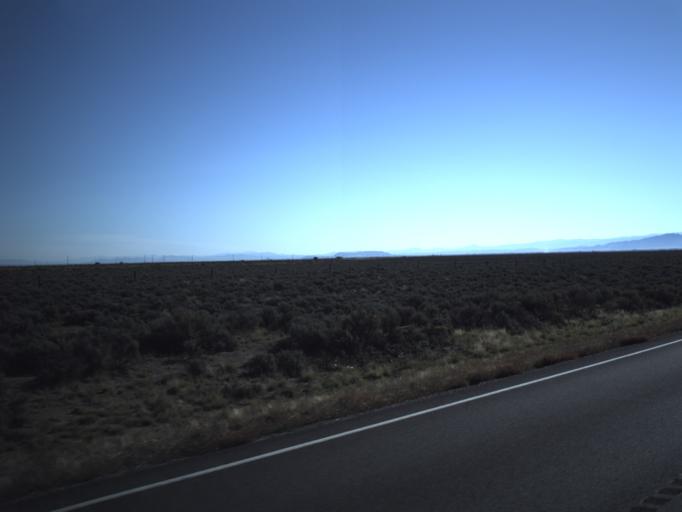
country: US
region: Utah
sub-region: Washington County
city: Enterprise
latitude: 37.7912
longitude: -113.8898
